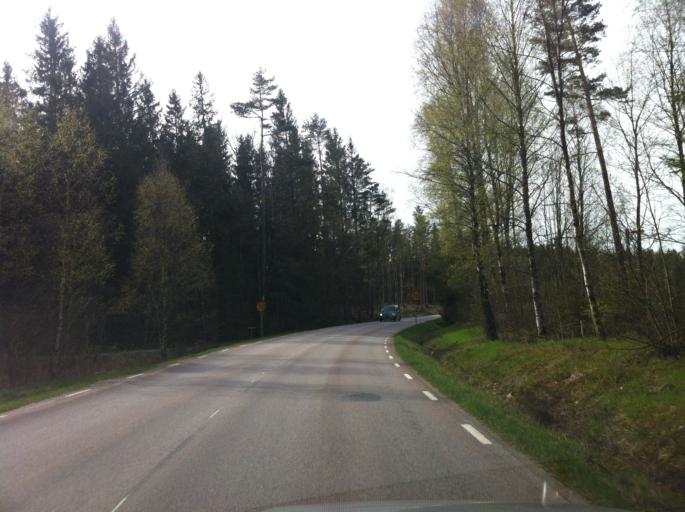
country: SE
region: Vaestra Goetaland
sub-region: Bollebygds Kommun
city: Bollebygd
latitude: 57.7088
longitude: 12.5823
